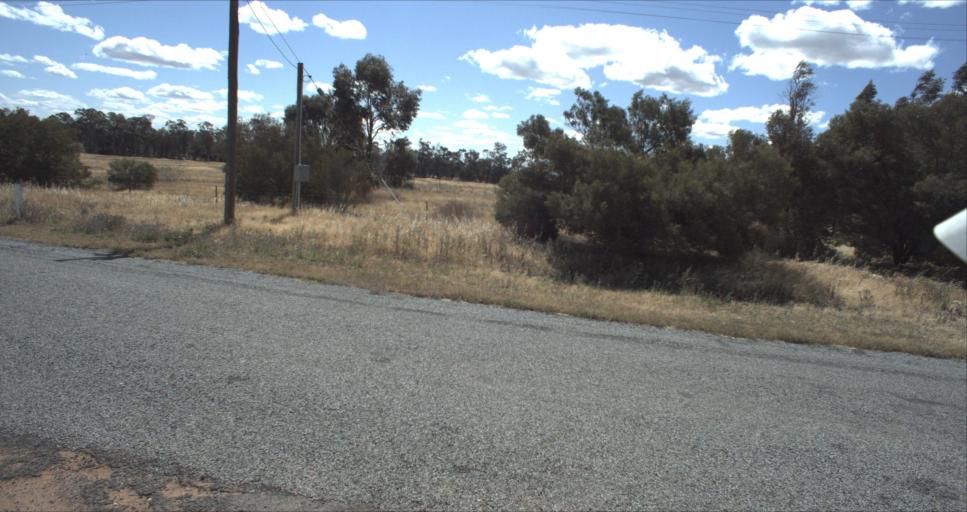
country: AU
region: New South Wales
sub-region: Leeton
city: Leeton
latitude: -34.5169
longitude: 146.2298
